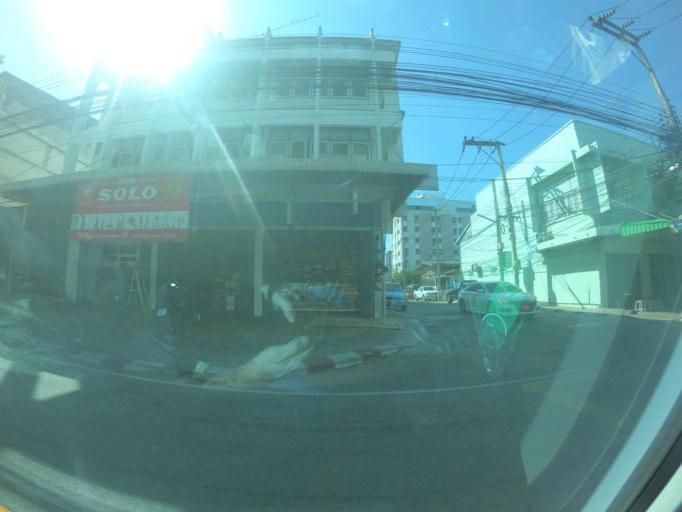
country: TH
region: Khon Kaen
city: Sam Sung
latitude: 16.4942
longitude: 102.9643
